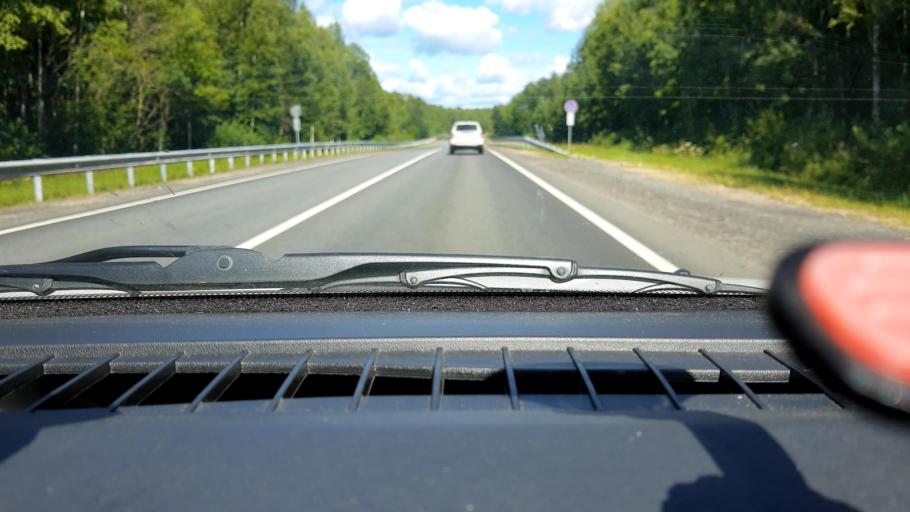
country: RU
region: Nizjnij Novgorod
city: Arzamas
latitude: 55.4494
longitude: 43.8845
